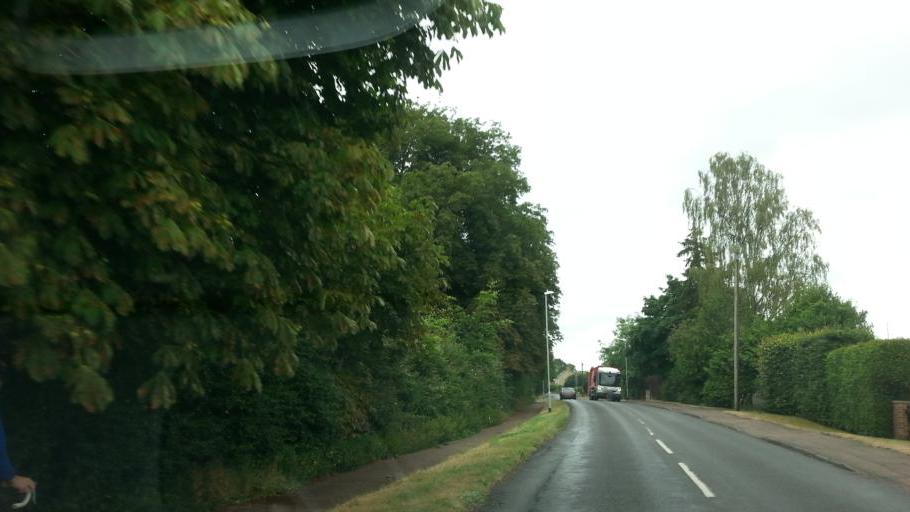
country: GB
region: England
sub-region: Cambridgeshire
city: Histon
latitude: 52.2546
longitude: 0.0947
